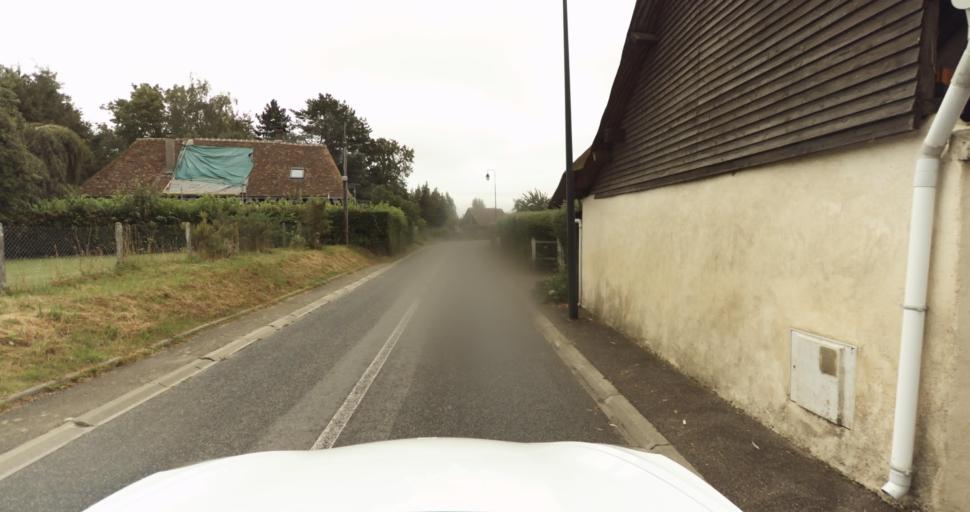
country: FR
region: Haute-Normandie
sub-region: Departement de l'Eure
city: Aviron
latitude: 49.0797
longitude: 1.0681
